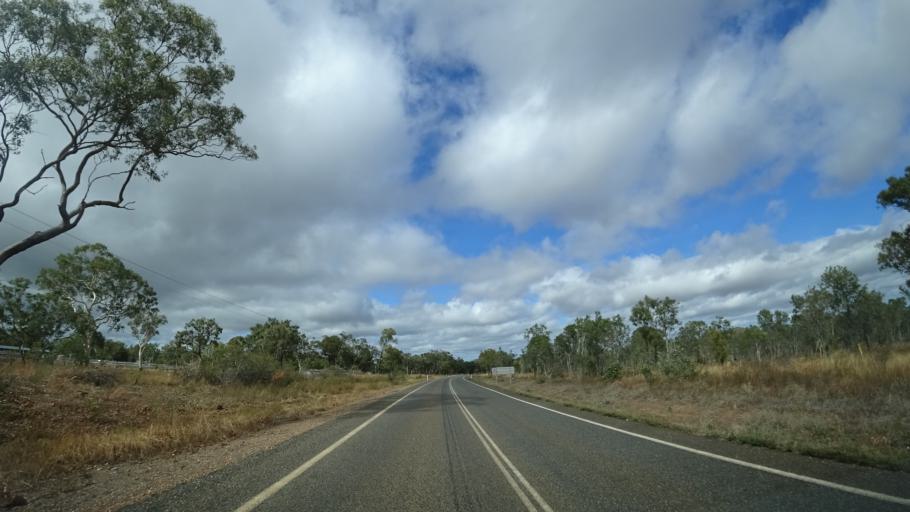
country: AU
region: Queensland
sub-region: Cook
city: Cooktown
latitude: -15.8727
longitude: 144.8607
